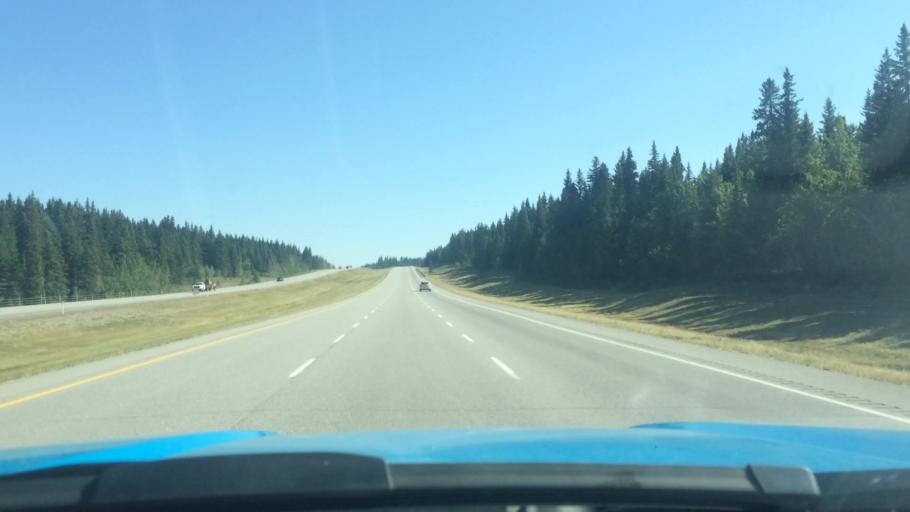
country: CA
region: Alberta
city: Cochrane
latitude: 51.1541
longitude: -114.7460
